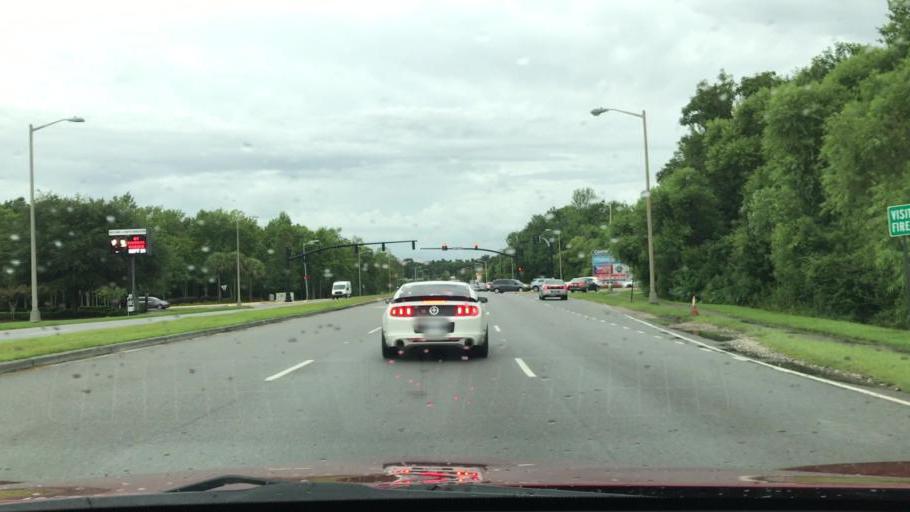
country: US
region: South Carolina
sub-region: Charleston County
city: North Charleston
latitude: 32.8674
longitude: -80.0200
